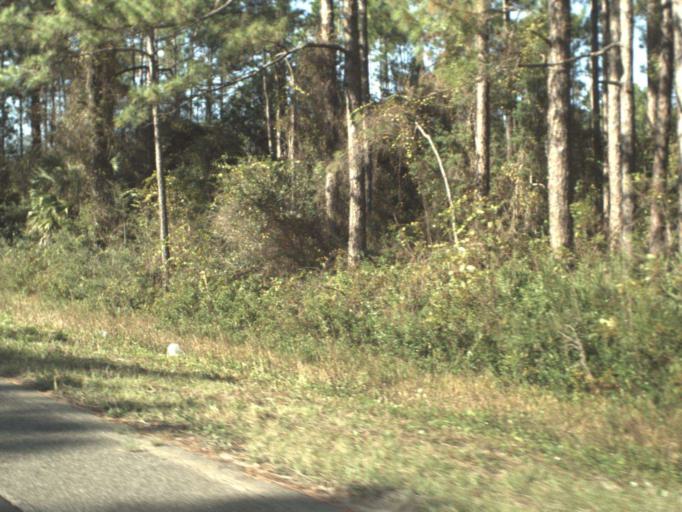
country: US
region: Florida
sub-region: Franklin County
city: Apalachicola
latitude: 29.7342
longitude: -85.1509
